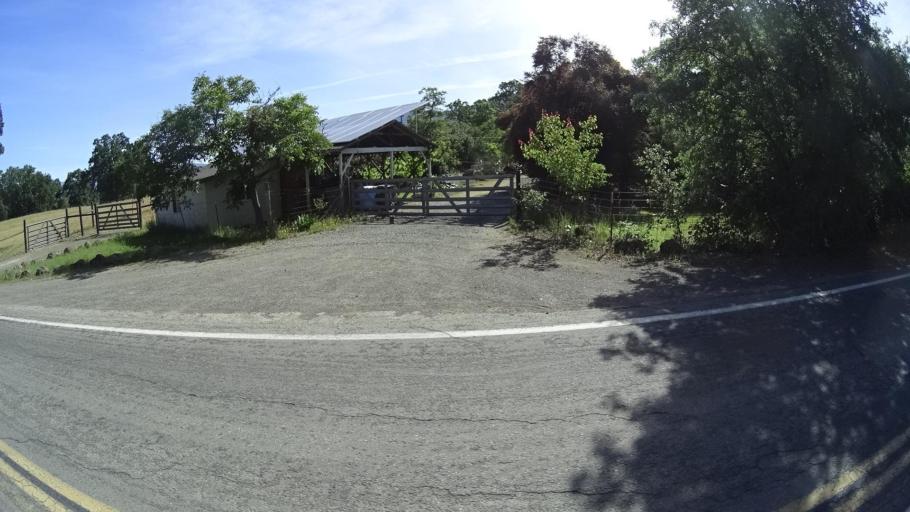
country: US
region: California
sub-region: Lake County
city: Kelseyville
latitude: 38.9632
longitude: -122.8375
